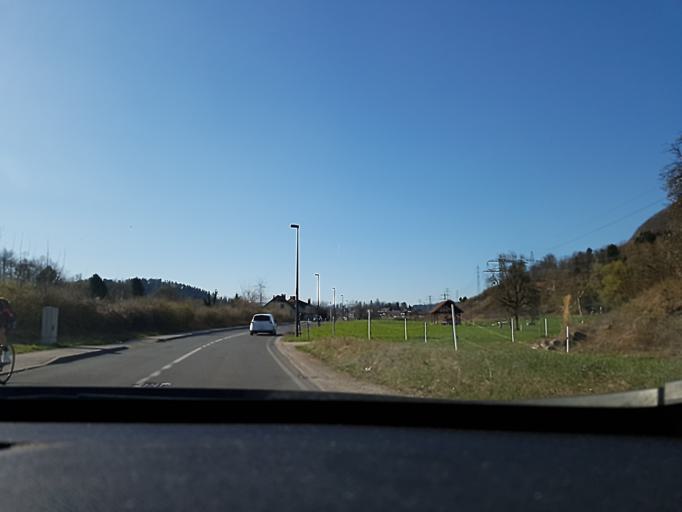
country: SI
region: Medvode
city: Zgornje Pirnice
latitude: 46.1192
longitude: 14.4508
